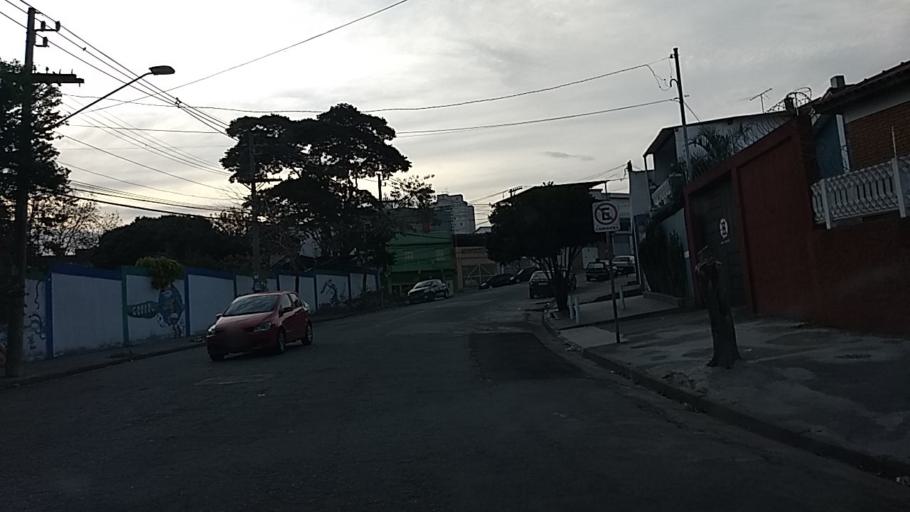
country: BR
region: Sao Paulo
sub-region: Guarulhos
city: Guarulhos
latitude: -23.5084
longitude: -46.5766
